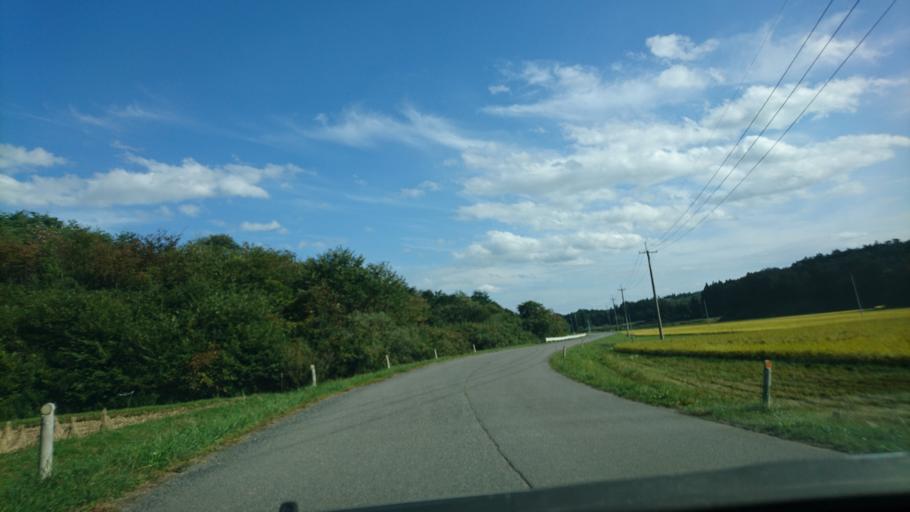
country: JP
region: Iwate
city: Ichinoseki
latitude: 38.8791
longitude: 141.0666
